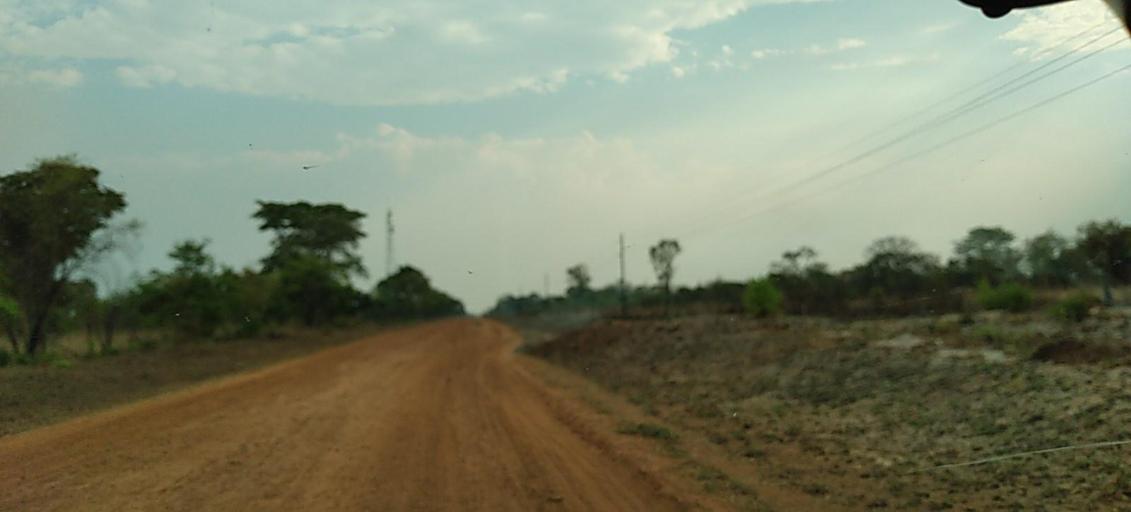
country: ZM
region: North-Western
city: Kabompo
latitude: -13.8811
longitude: 23.6638
